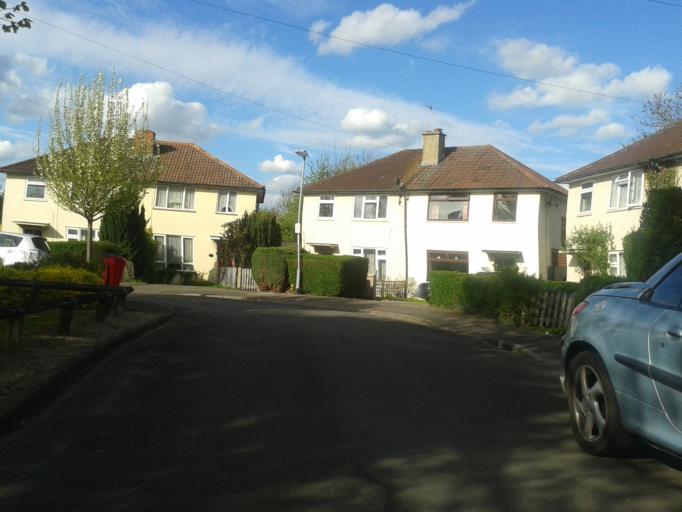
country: GB
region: England
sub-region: Cambridgeshire
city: Cambridge
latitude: 52.1885
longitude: 0.1615
